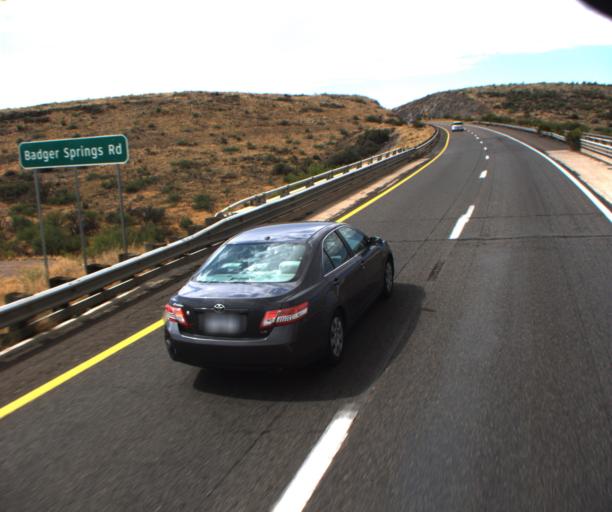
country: US
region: Arizona
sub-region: Yavapai County
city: Cordes Lakes
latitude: 34.2360
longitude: -112.1168
